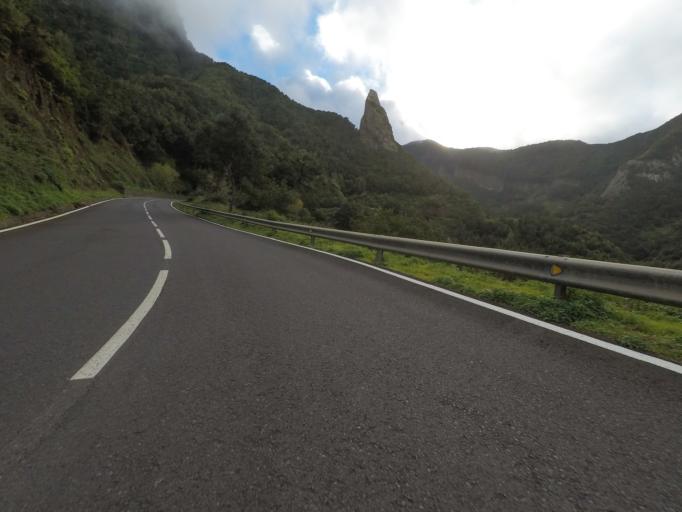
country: ES
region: Canary Islands
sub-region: Provincia de Santa Cruz de Tenerife
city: Hermigua
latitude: 28.1327
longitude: -17.2018
